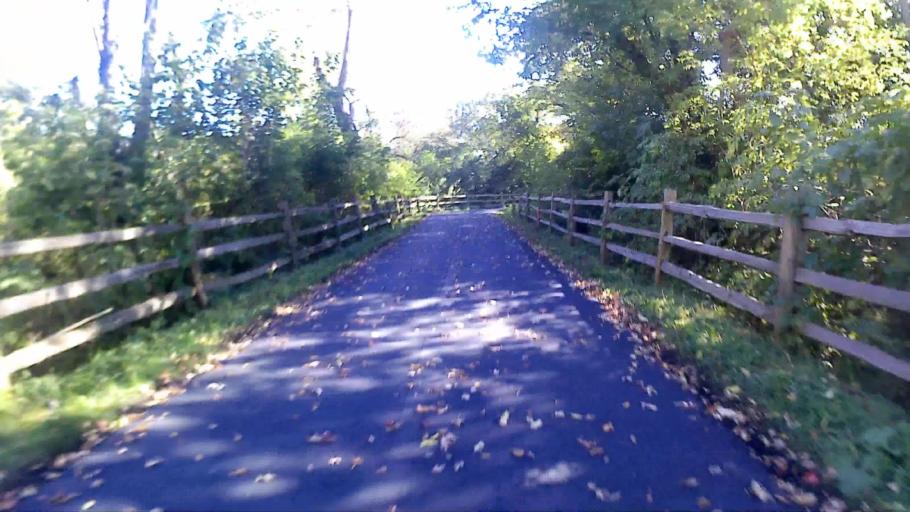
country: US
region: Illinois
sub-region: DuPage County
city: Villa Park
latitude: 41.9043
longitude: -87.9674
